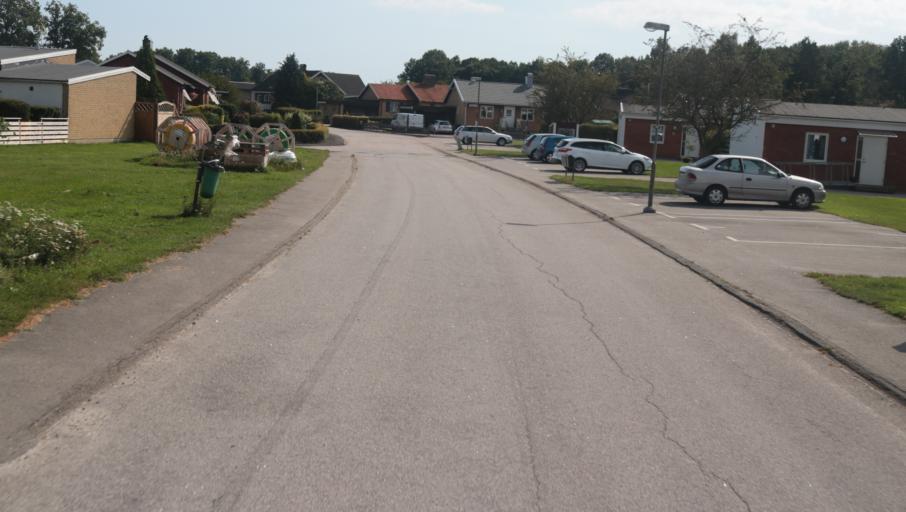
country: SE
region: Blekinge
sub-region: Karlshamns Kommun
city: Morrum
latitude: 56.2007
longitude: 14.7399
